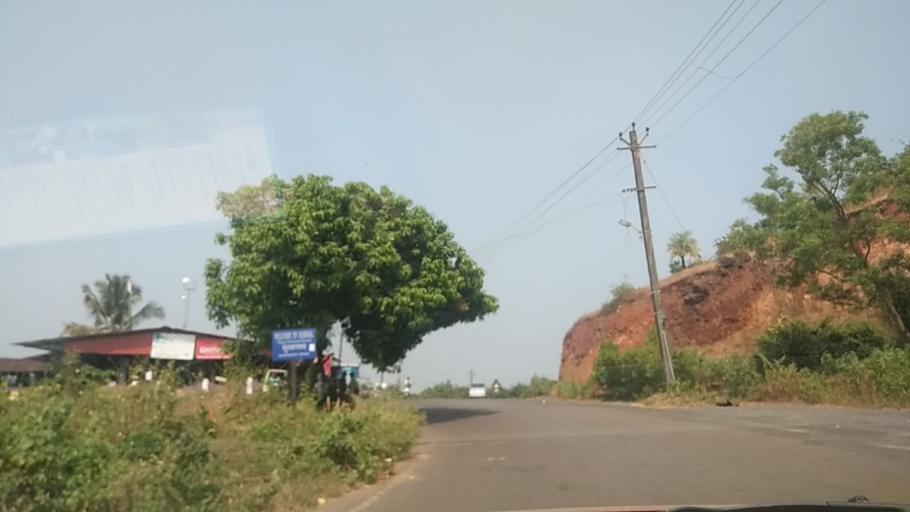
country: IN
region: Goa
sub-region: North Goa
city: Arambol
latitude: 15.6740
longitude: 73.7093
